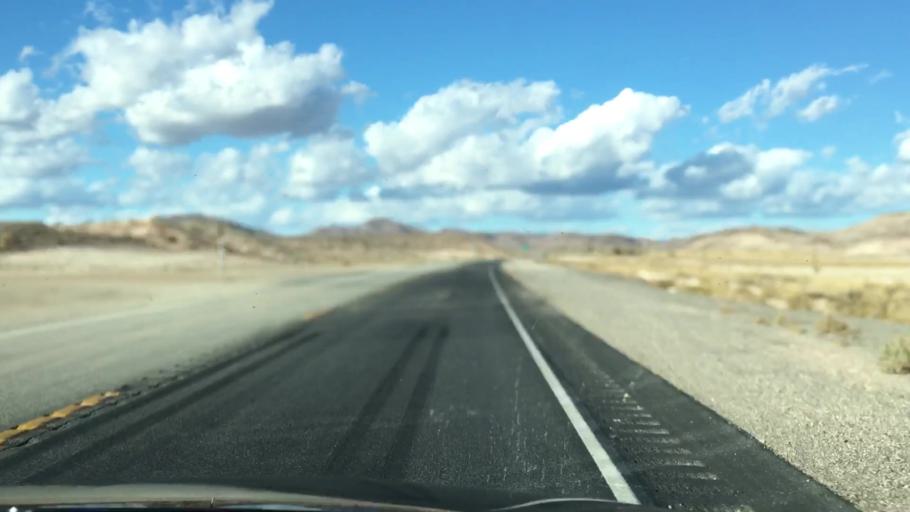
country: US
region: Nevada
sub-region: Nye County
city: Beatty
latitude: 36.9894
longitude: -116.7252
